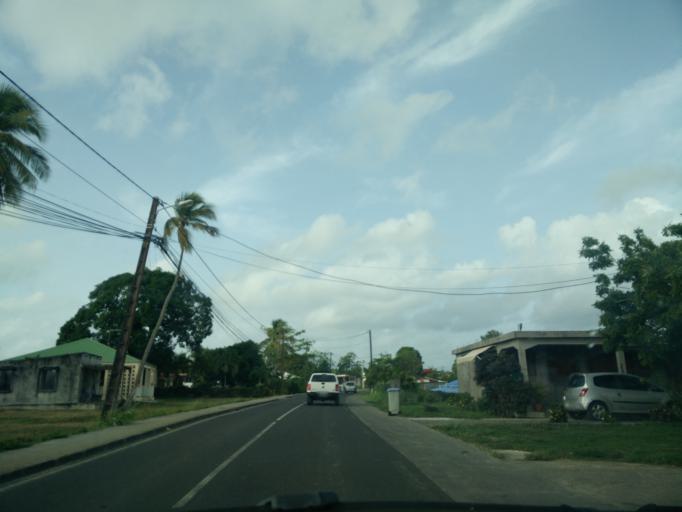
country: GP
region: Guadeloupe
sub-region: Guadeloupe
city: Le Moule
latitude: 16.2945
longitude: -61.3677
